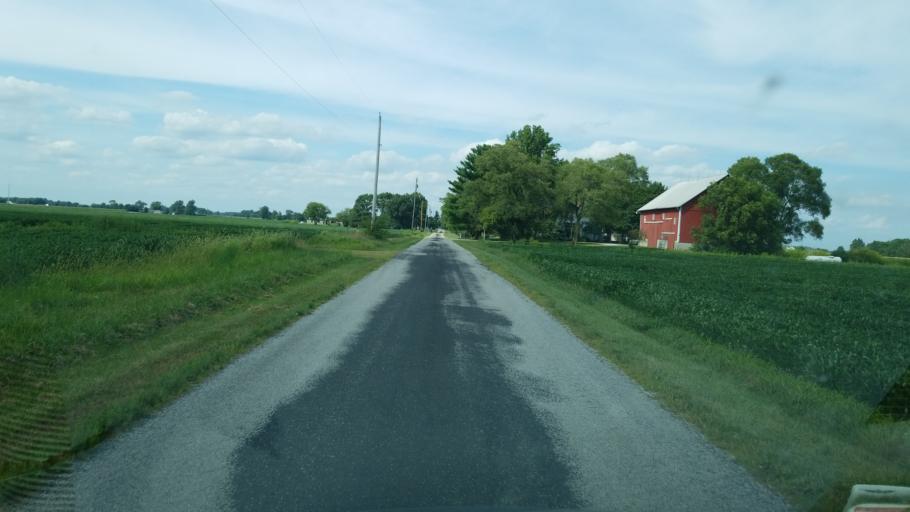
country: US
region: Ohio
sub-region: Marion County
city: Prospect
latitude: 40.4629
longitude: -83.1247
